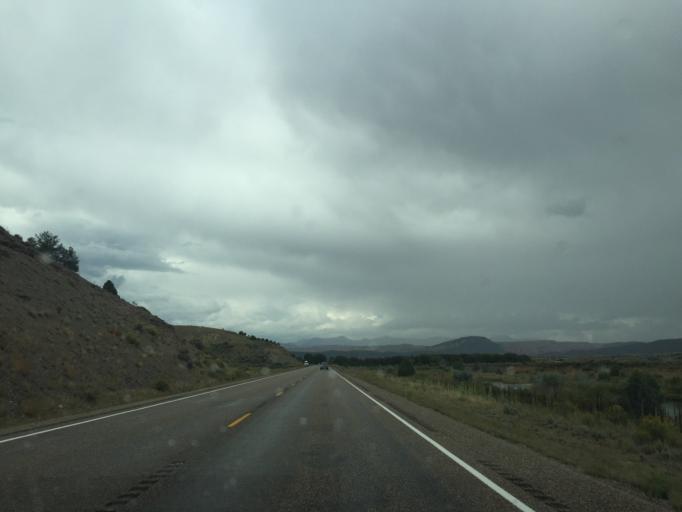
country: US
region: Utah
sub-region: Garfield County
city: Panguitch
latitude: 37.7061
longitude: -112.3938
